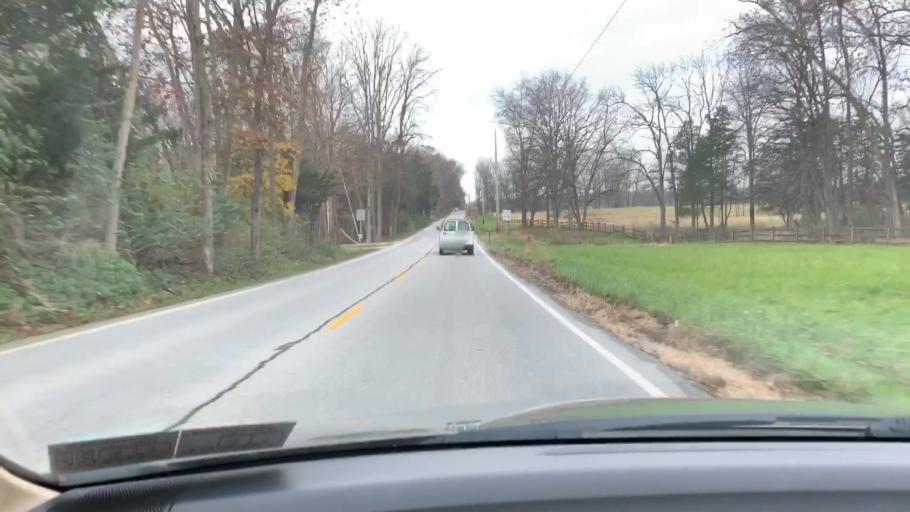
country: US
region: Pennsylvania
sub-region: Adams County
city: Lake Meade
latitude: 39.9419
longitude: -77.0732
